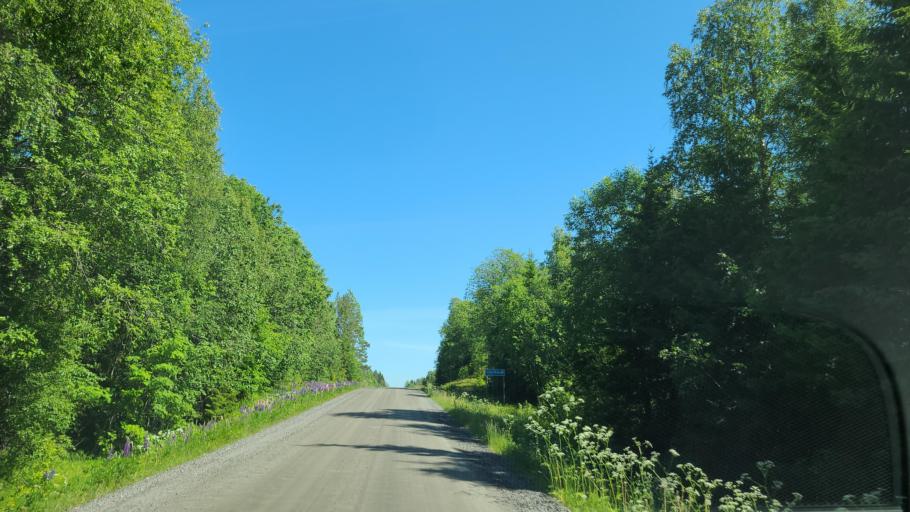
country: SE
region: Vaesterbotten
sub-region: Bjurholms Kommun
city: Bjurholm
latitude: 63.6419
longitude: 19.1300
